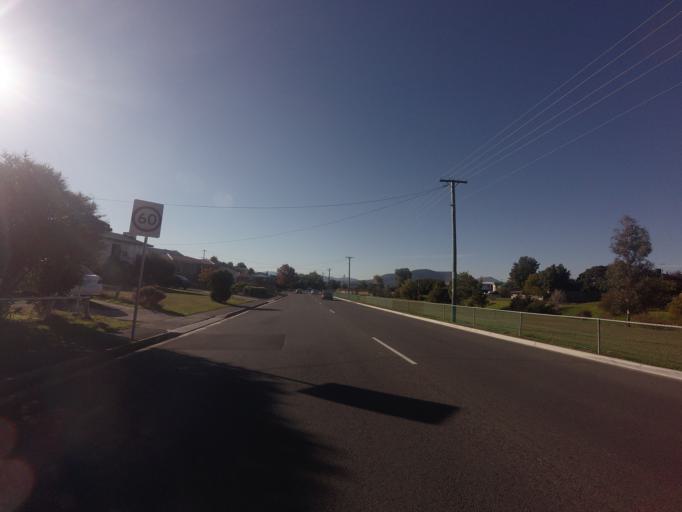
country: AU
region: Tasmania
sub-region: Glenorchy
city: West Moonah
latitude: -42.8467
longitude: 147.2671
